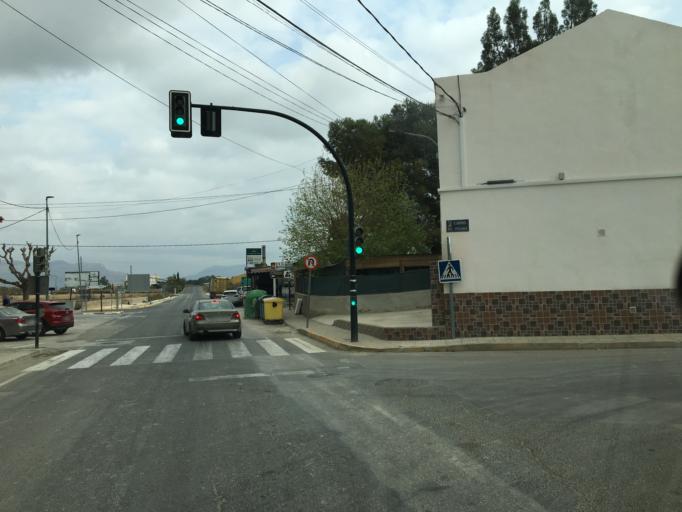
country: ES
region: Murcia
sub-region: Murcia
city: Beniel
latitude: 38.0280
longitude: -0.9799
